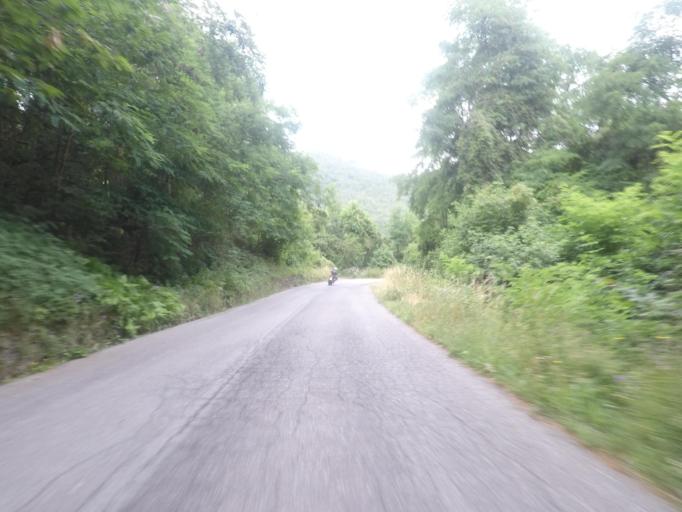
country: IT
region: Tuscany
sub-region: Provincia di Lucca
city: Careggine
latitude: 44.1156
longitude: 10.3595
